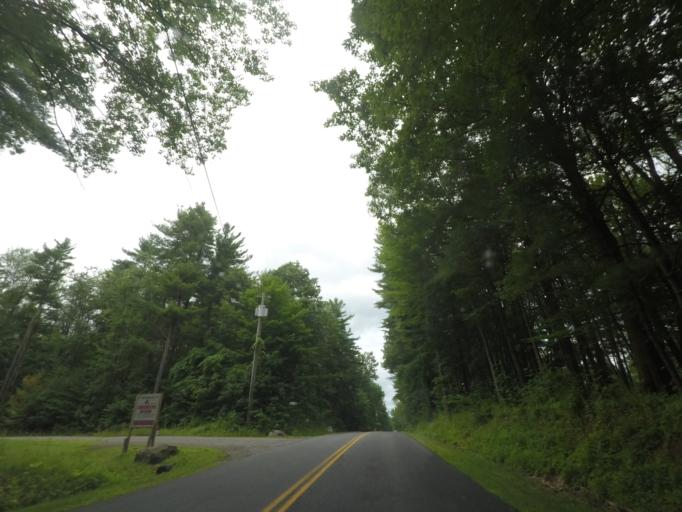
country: US
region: New York
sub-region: Saratoga County
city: Stillwater
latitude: 42.9953
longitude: -73.6921
